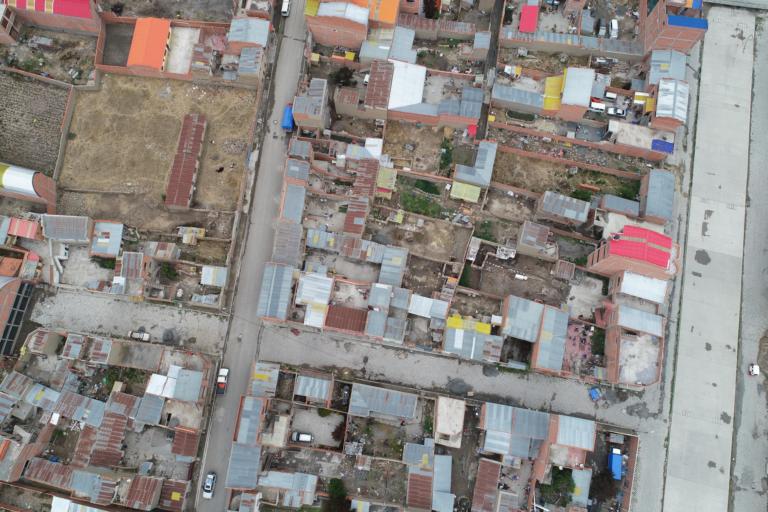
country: BO
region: La Paz
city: Achacachi
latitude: -16.0479
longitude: -68.6843
